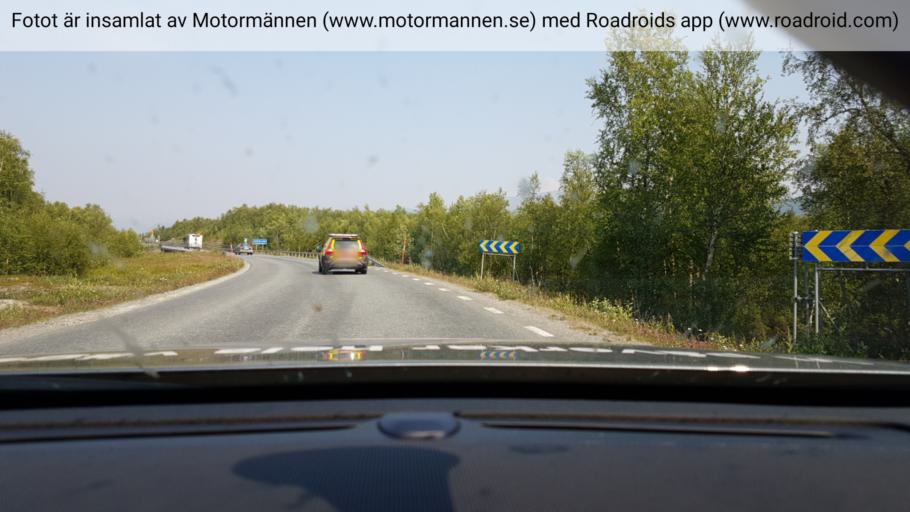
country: NO
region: Nordland
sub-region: Rana
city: Mo i Rana
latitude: 65.7800
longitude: 15.1130
